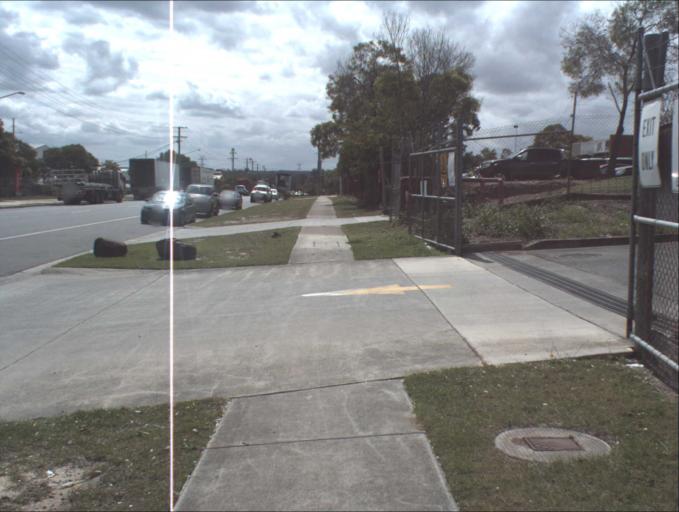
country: AU
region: Queensland
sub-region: Logan
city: Logan Reserve
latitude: -27.6839
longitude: 153.0705
